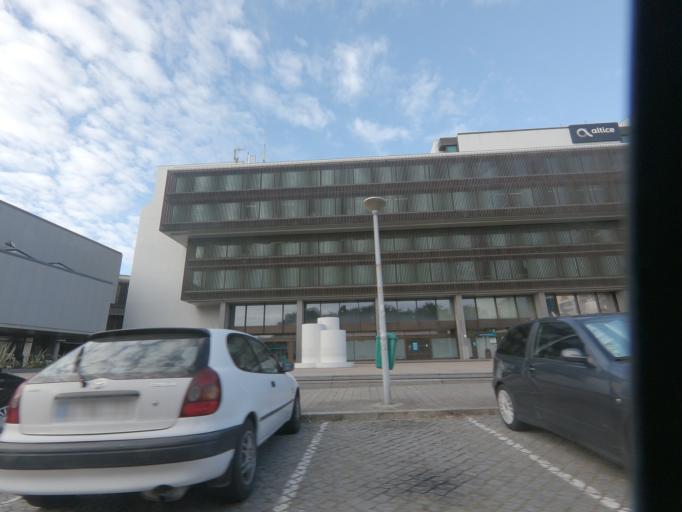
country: PT
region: Porto
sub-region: Matosinhos
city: Senhora da Hora
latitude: 41.1632
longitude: -8.6394
